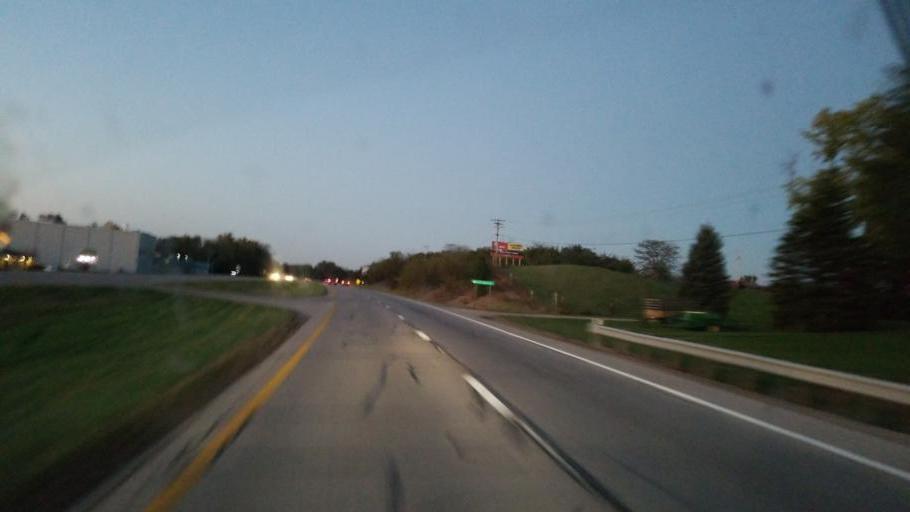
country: US
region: Ohio
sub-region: Pickaway County
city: Logan Elm Village
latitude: 39.5194
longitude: -82.9692
